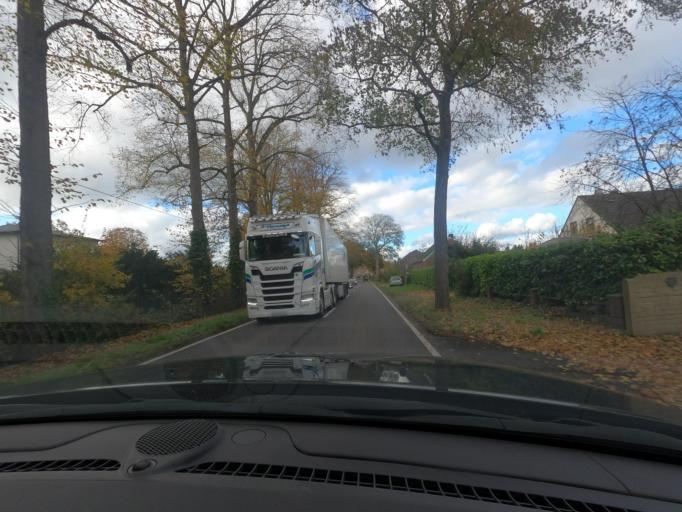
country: DE
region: North Rhine-Westphalia
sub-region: Regierungsbezirk Dusseldorf
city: Schwalmtal
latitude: 51.2551
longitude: 6.3003
